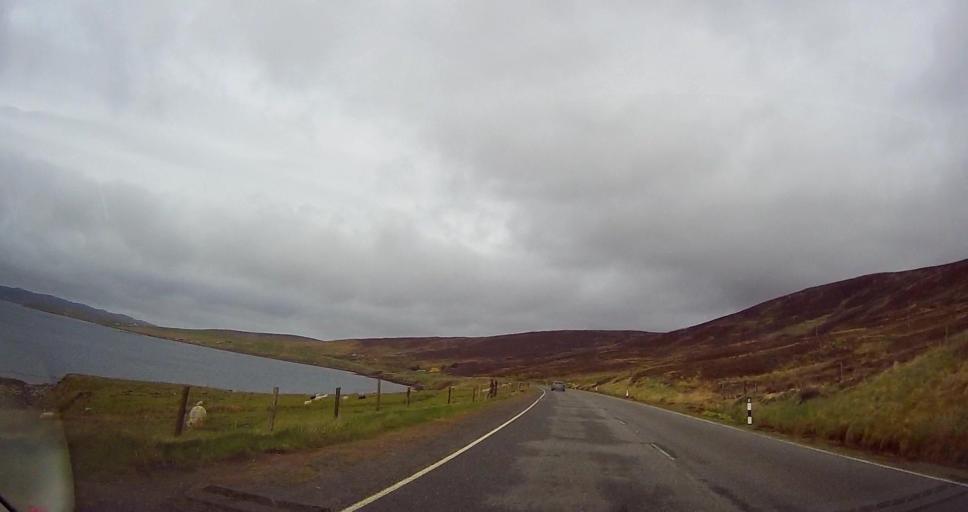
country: GB
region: Scotland
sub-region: Shetland Islands
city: Lerwick
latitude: 60.3648
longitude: -1.2884
